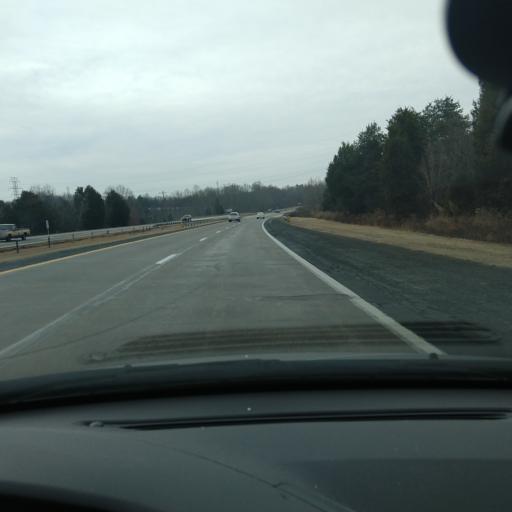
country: US
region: North Carolina
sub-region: Davidson County
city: Midway
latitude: 36.0168
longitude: -80.2357
